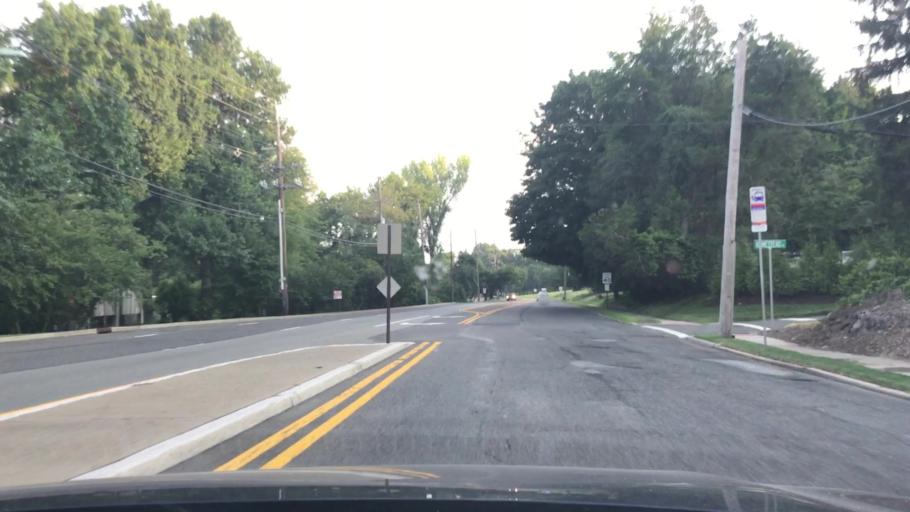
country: US
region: New Jersey
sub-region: Bergen County
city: Emerson
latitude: 40.9668
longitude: -74.0301
